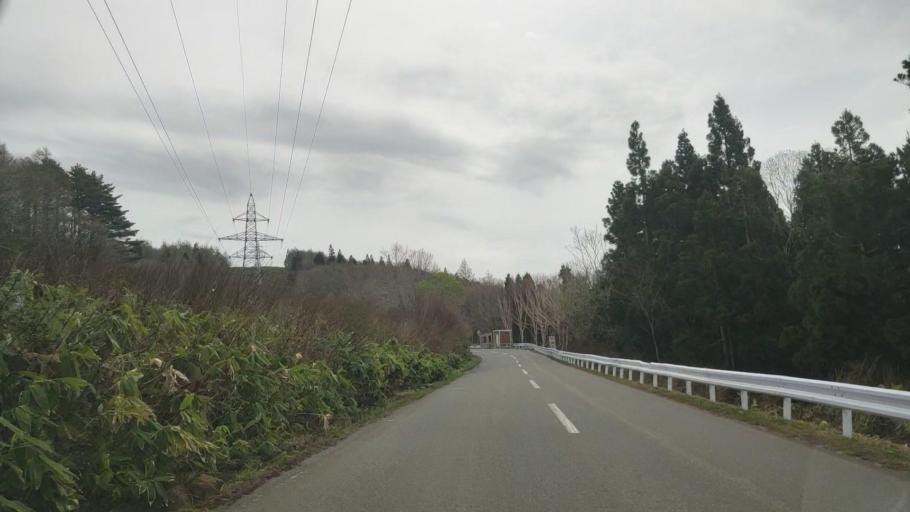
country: JP
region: Aomori
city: Aomori Shi
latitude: 40.7181
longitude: 140.8658
